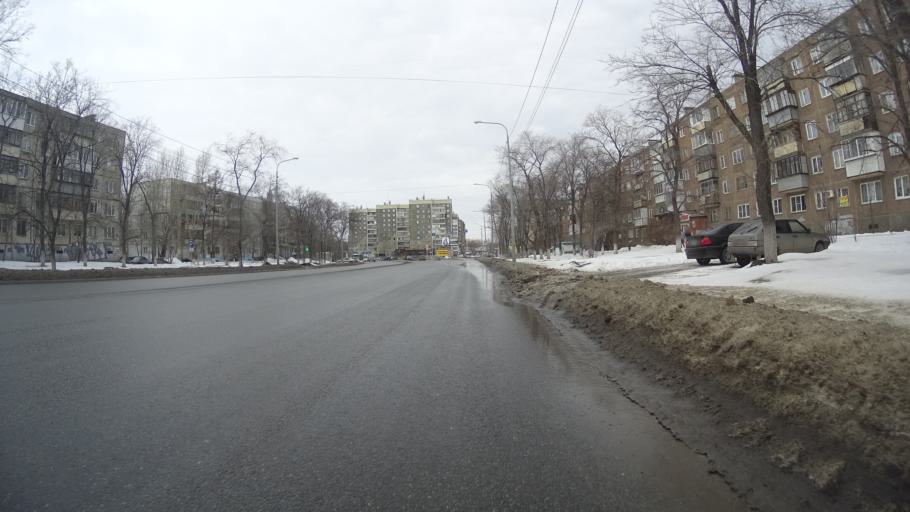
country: RU
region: Chelyabinsk
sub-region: Gorod Chelyabinsk
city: Chelyabinsk
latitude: 55.1968
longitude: 61.3329
